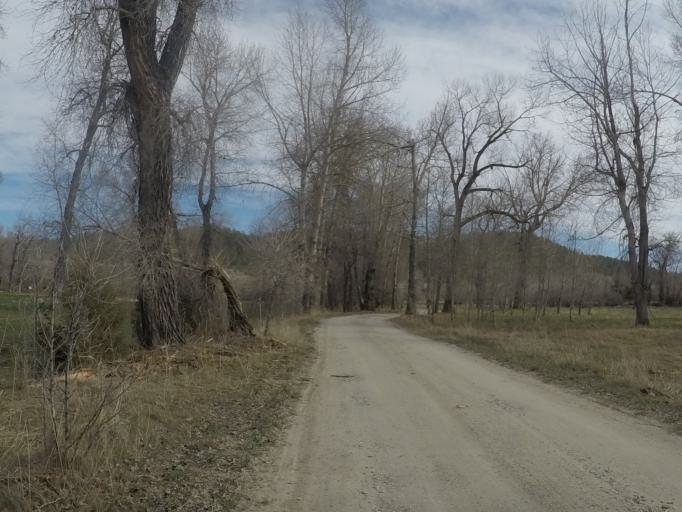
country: US
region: Montana
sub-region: Stillwater County
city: Columbus
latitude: 45.5833
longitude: -109.3316
